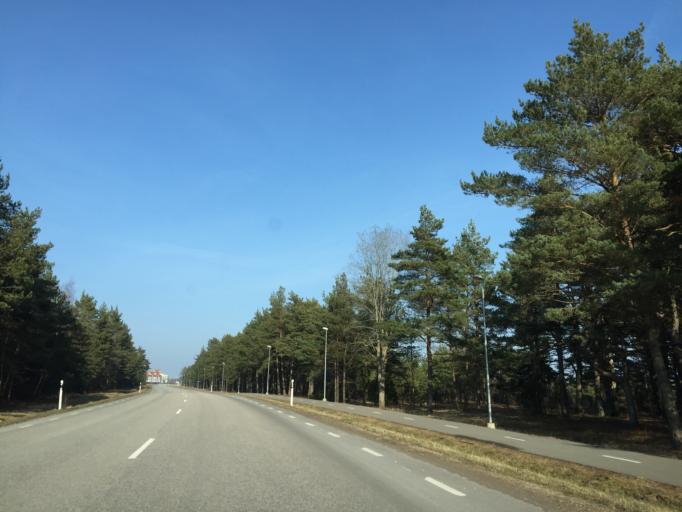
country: EE
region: Saare
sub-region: Kuressaare linn
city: Kuressaare
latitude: 58.2419
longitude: 22.4501
